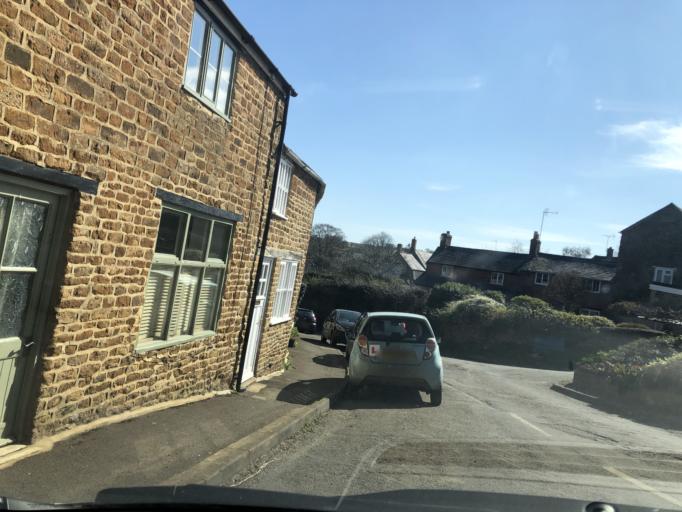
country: GB
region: England
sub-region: Oxfordshire
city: Hook Norton
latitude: 51.9958
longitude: -1.4826
